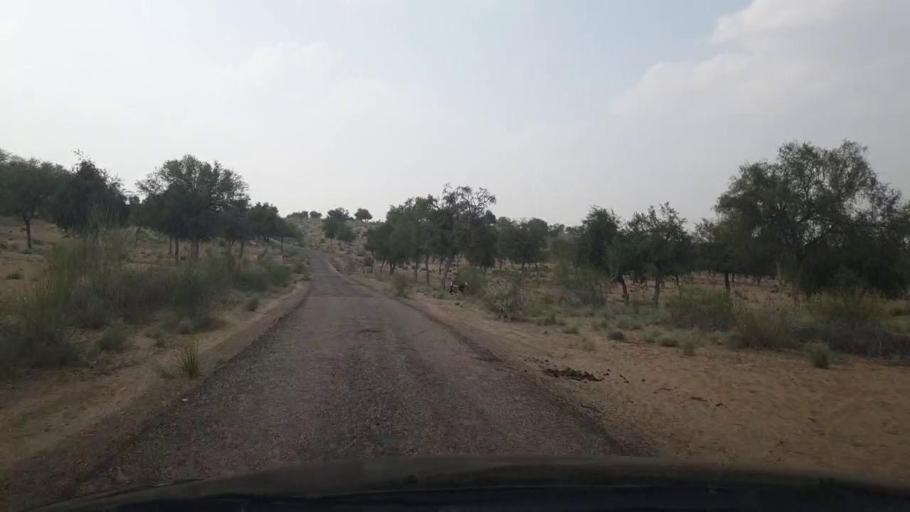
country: PK
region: Sindh
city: Islamkot
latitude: 24.9675
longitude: 70.6012
